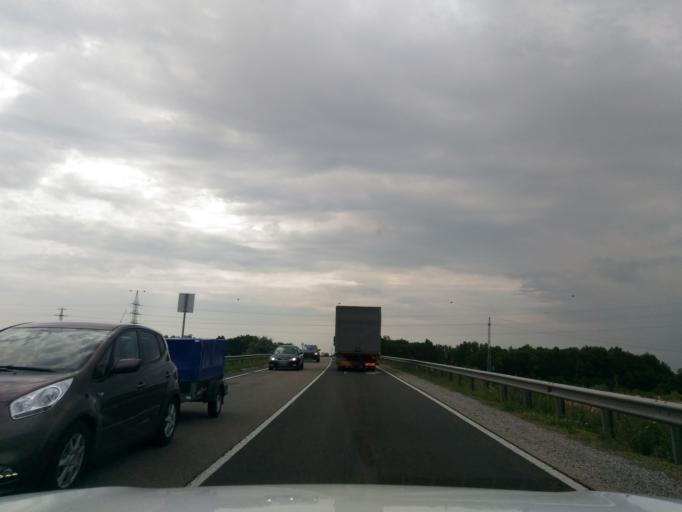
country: HU
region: Jasz-Nagykun-Szolnok
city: Toszeg
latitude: 47.1520
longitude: 20.1306
